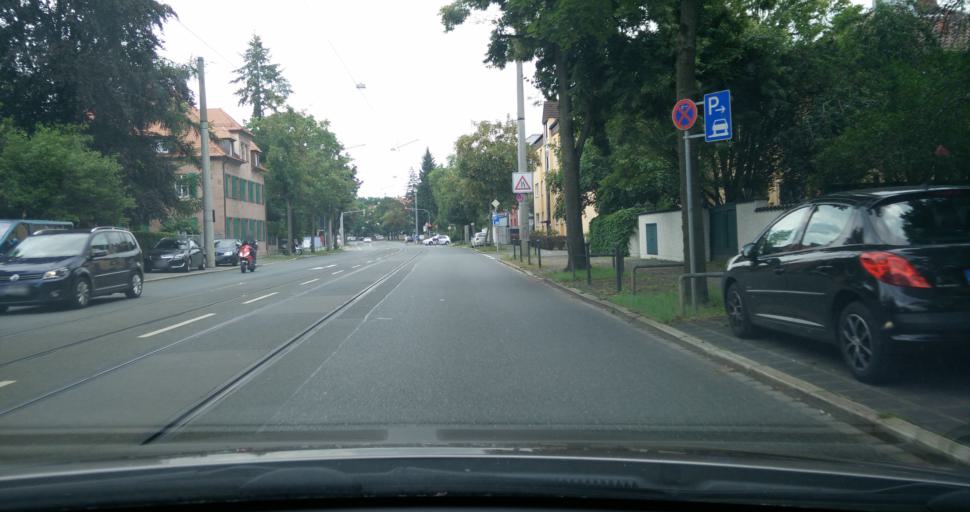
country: DE
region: Bavaria
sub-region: Regierungsbezirk Mittelfranken
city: Nuernberg
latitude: 49.4578
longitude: 11.1327
